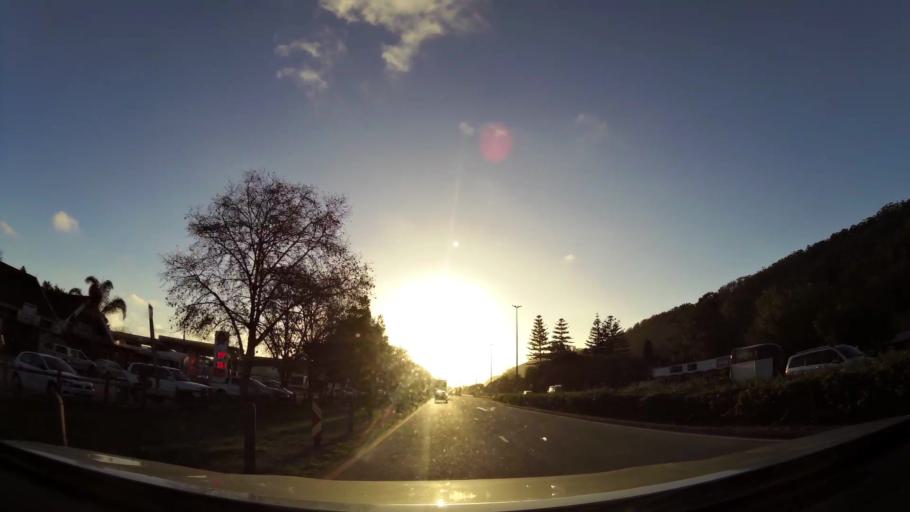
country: ZA
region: Western Cape
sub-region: Eden District Municipality
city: Knysna
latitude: -34.0152
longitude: 22.8039
